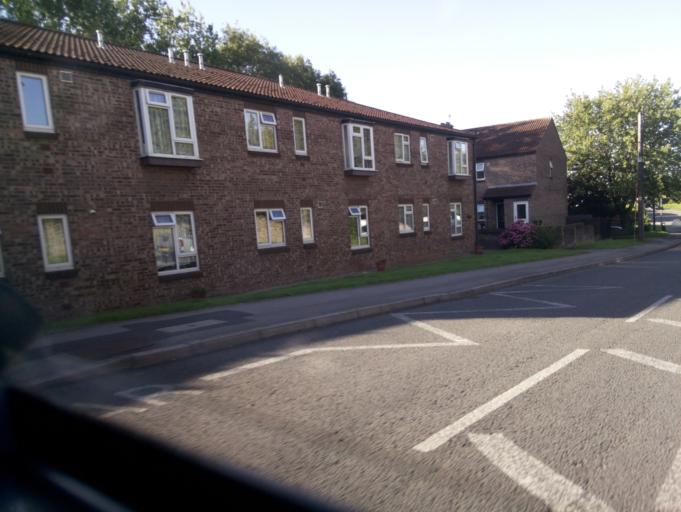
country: GB
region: England
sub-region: South Gloucestershire
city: Kingswood
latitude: 51.4478
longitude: -2.5217
